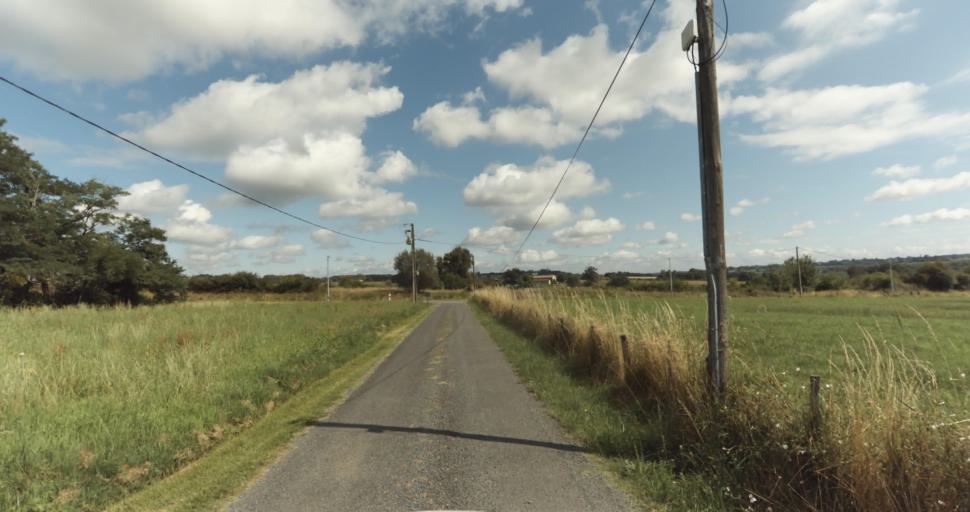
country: FR
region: Aquitaine
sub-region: Departement de la Gironde
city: Bazas
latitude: 44.4411
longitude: -0.1765
